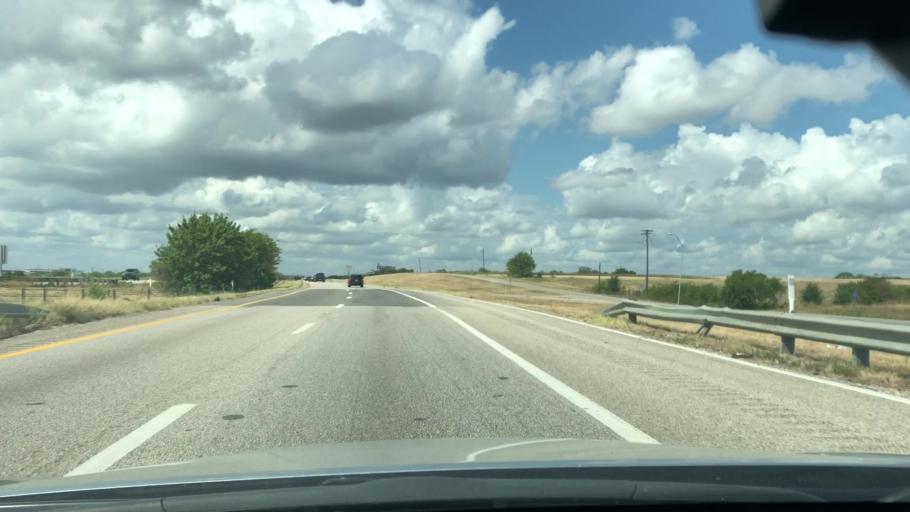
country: US
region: Texas
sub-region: Guadalupe County
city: McQueeney
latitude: 29.5608
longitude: -98.0326
